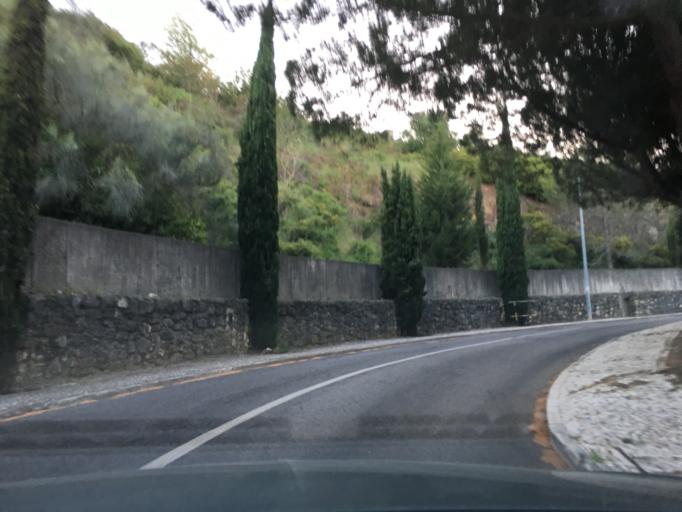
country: PT
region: Lisbon
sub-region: Oeiras
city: Quejas
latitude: 38.7174
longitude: -9.2781
